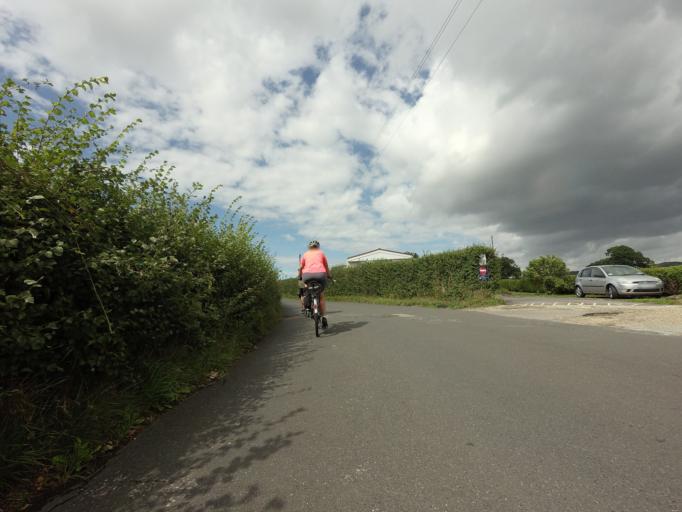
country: GB
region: England
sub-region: Kent
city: Sevenoaks
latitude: 51.2976
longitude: 0.1780
